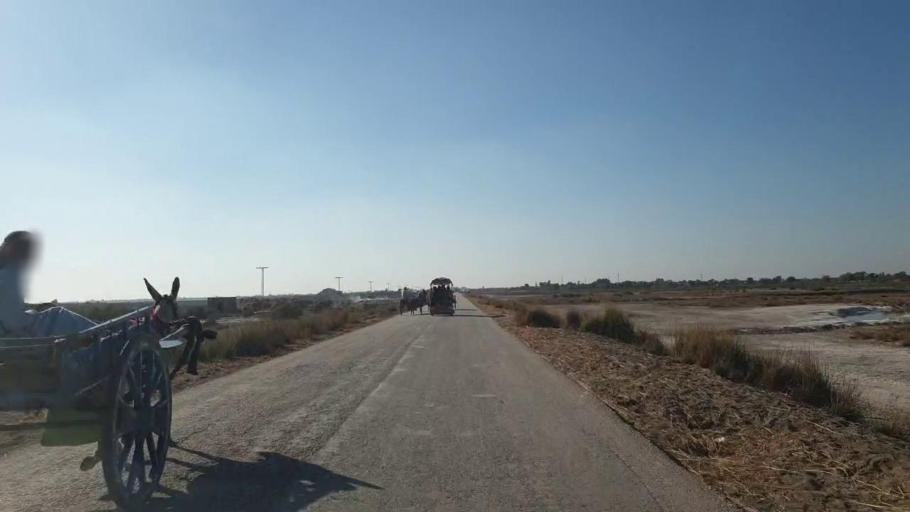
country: PK
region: Sindh
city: New Badah
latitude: 27.3250
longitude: 68.0501
